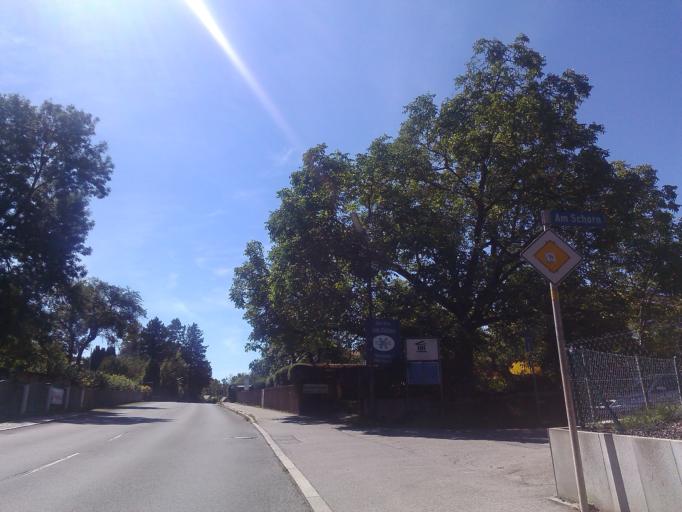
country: DE
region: Bavaria
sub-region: Upper Bavaria
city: Tutzing
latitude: 47.9206
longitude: 11.2879
